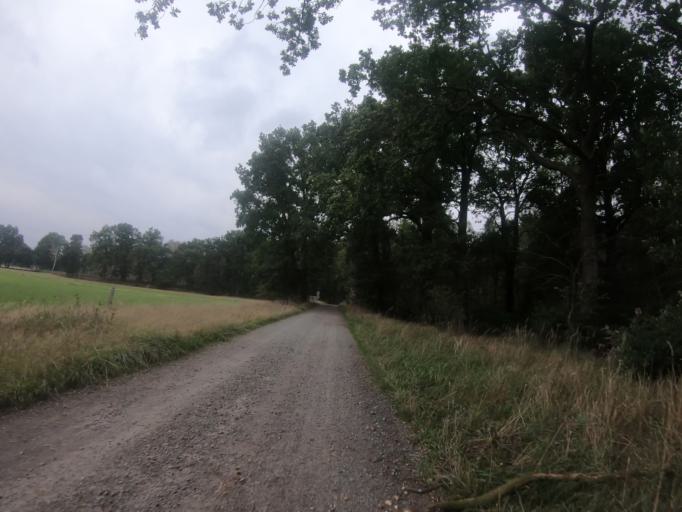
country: DE
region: Lower Saxony
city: Ribbesbuttel
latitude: 52.4507
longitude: 10.5242
